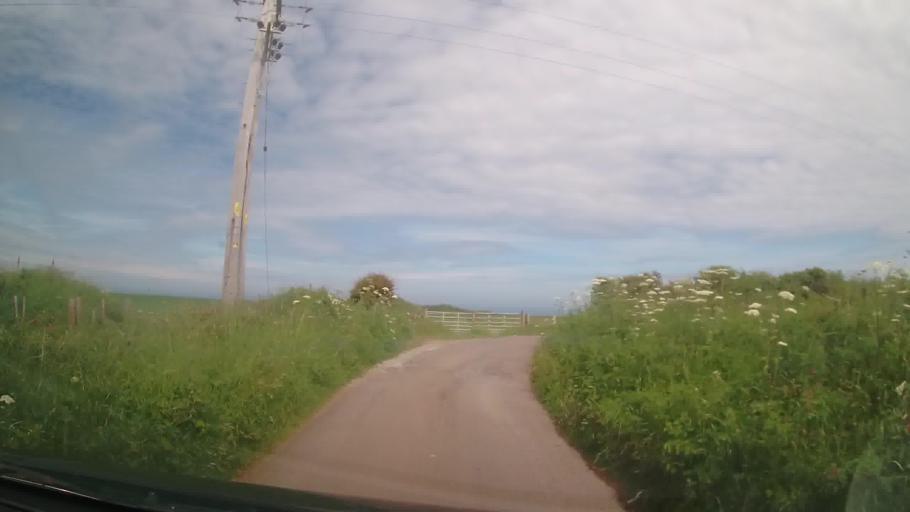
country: GB
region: England
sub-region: Devon
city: Salcombe
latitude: 50.2297
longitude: -3.6623
